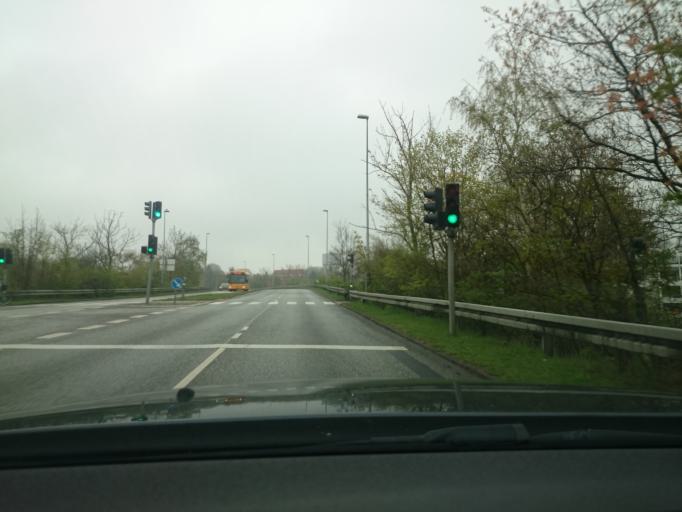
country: DK
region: Capital Region
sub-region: Ballerup Kommune
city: Ballerup
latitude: 55.7277
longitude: 12.3599
